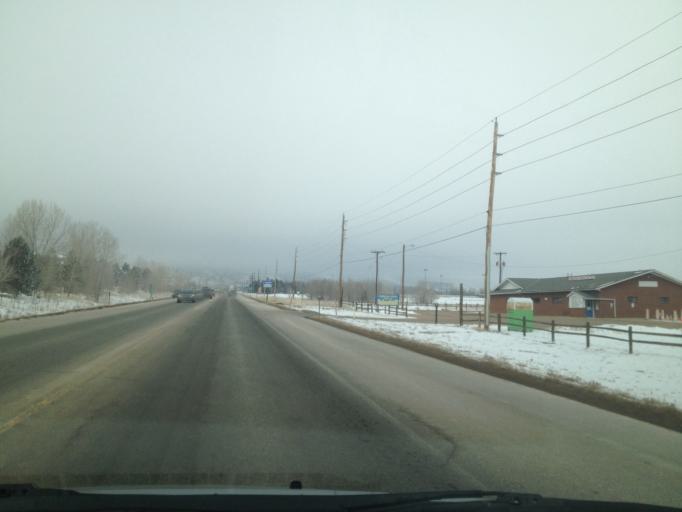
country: US
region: Colorado
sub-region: Boulder County
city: Boulder
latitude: 40.0597
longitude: -105.2732
